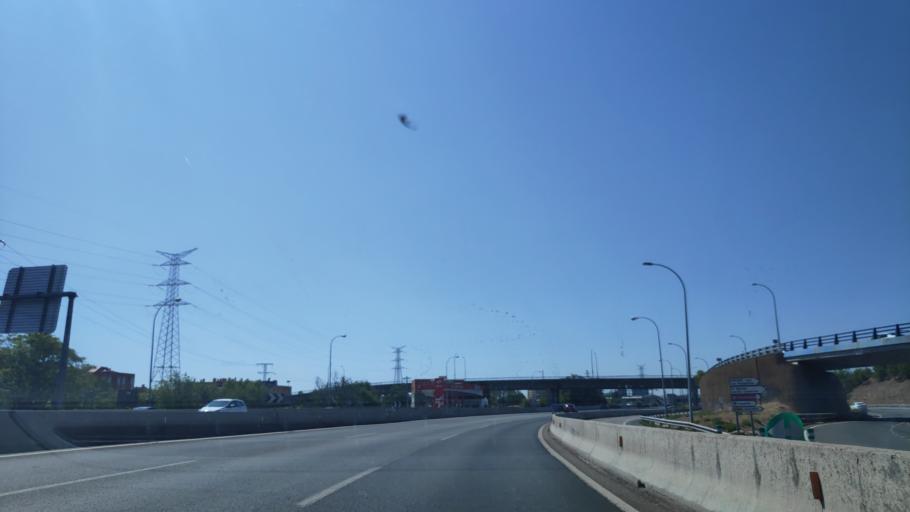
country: ES
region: Madrid
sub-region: Provincia de Madrid
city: Getafe
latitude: 40.3290
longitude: -3.7255
